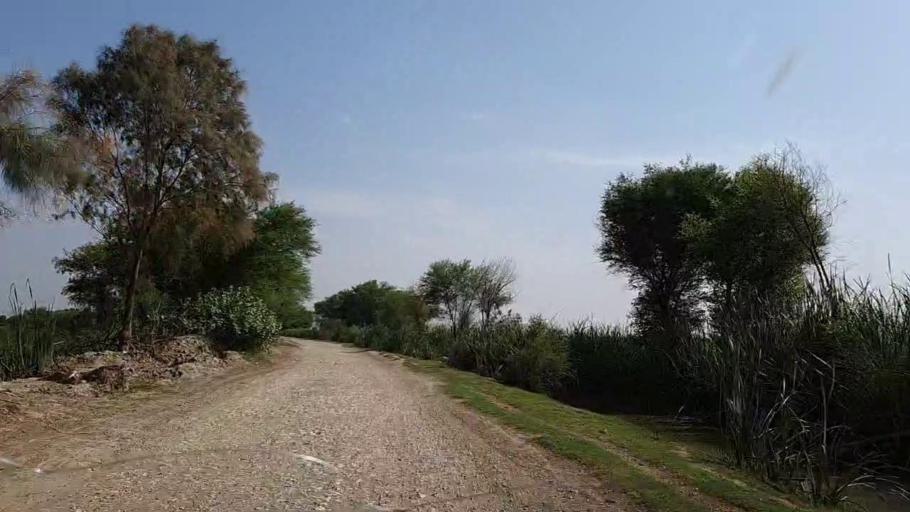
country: PK
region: Sindh
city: Khanpur
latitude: 27.7231
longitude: 69.3605
